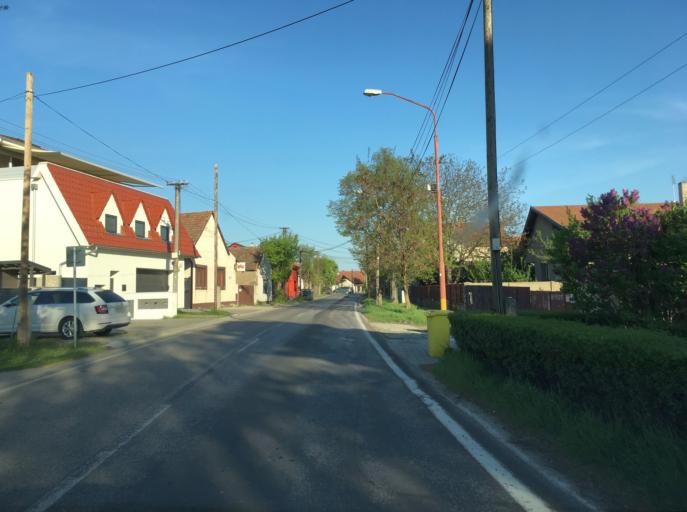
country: AT
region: Burgenland
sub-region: Politischer Bezirk Neusiedl am See
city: Deutsch Jahrndorf
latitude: 48.0573
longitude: 17.1412
